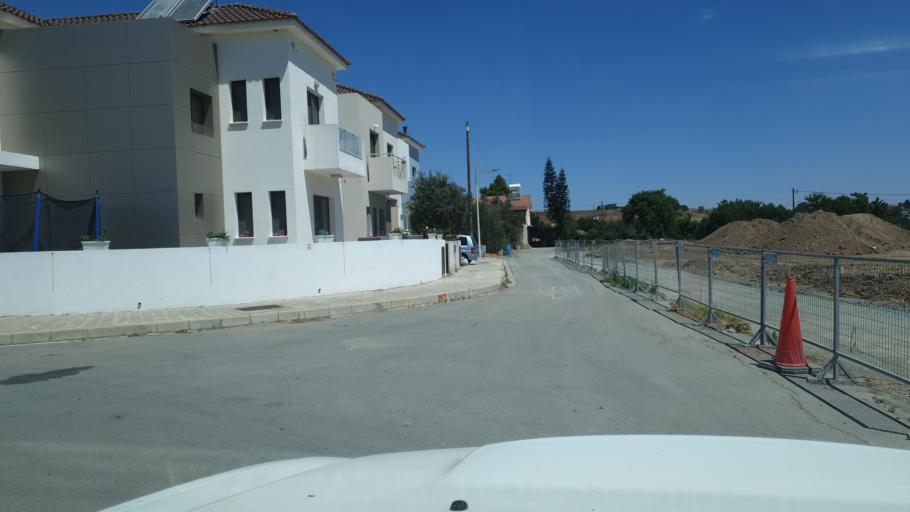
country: CY
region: Lefkosia
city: Dali
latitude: 35.0208
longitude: 33.4089
